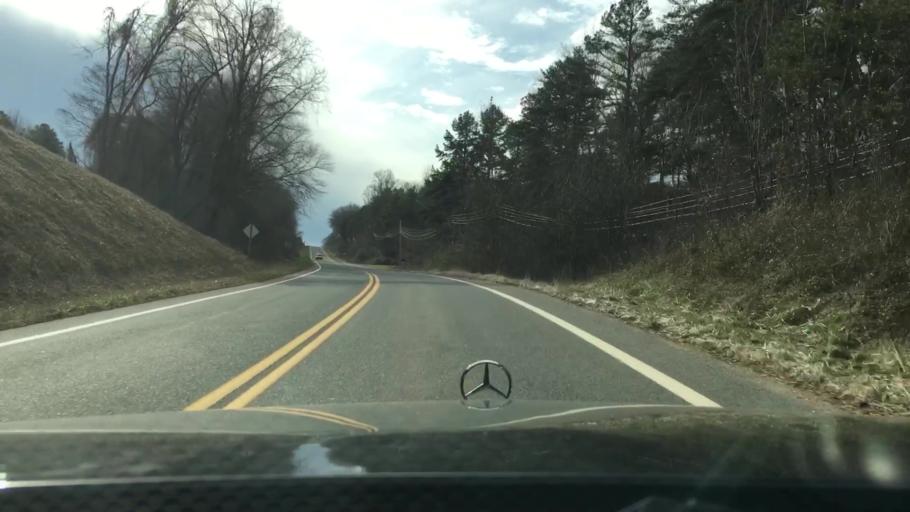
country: US
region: Virginia
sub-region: Pittsylvania County
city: Motley
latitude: 37.0875
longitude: -79.3227
